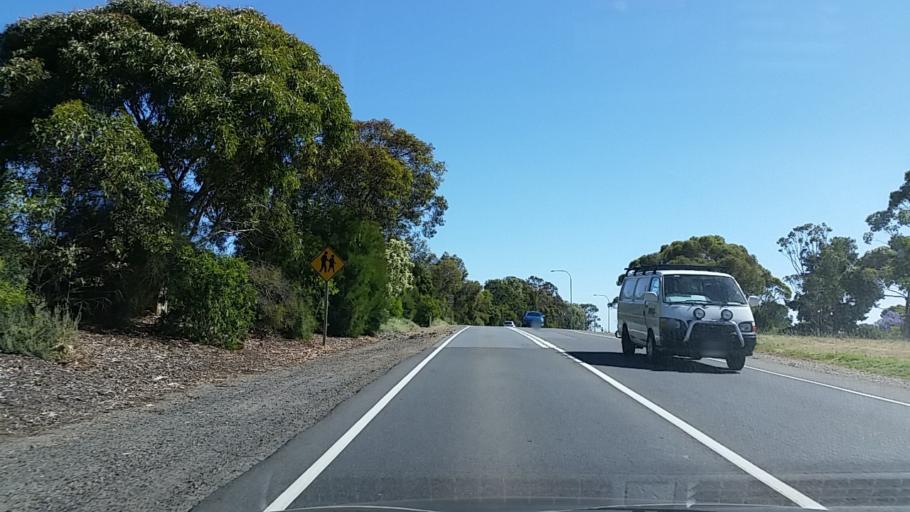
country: AU
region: South Australia
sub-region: Tea Tree Gully
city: Hope Valley
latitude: -34.8015
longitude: 138.7052
